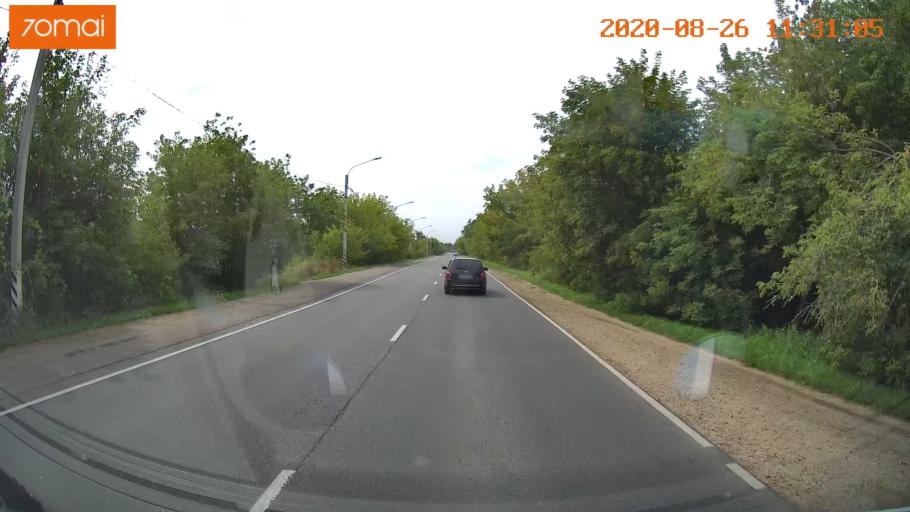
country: RU
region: Rjazan
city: Shilovo
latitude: 54.3098
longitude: 40.8765
